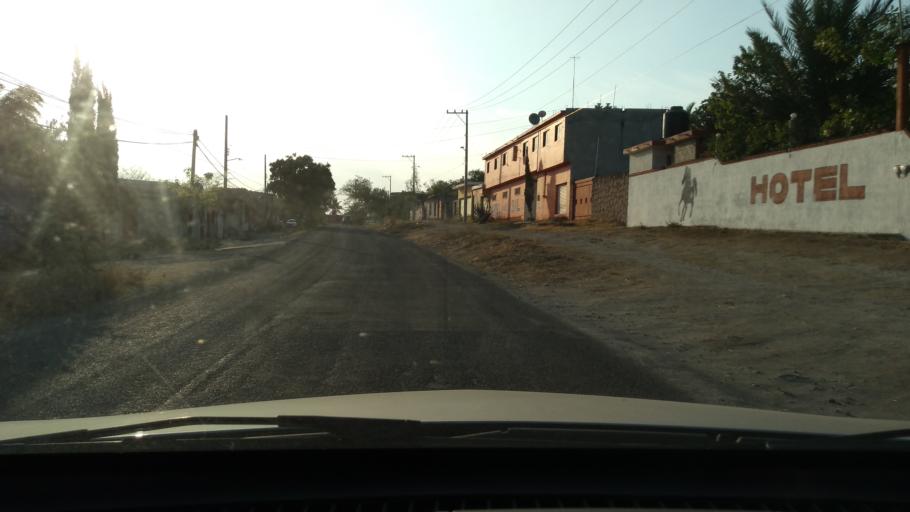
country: MX
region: Morelos
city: Puente de Ixtla
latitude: 18.6068
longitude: -99.3157
